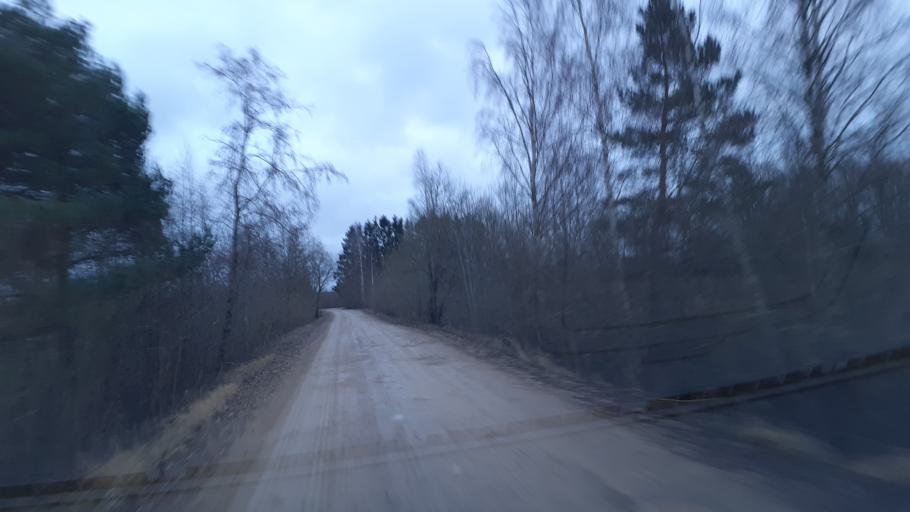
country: LV
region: Kuldigas Rajons
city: Kuldiga
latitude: 57.0456
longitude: 22.1326
